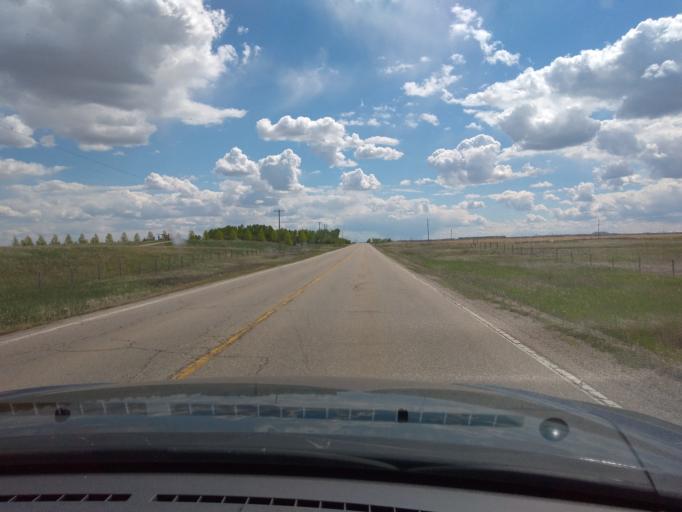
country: CA
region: Alberta
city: Chestermere
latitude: 50.9418
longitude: -113.9120
